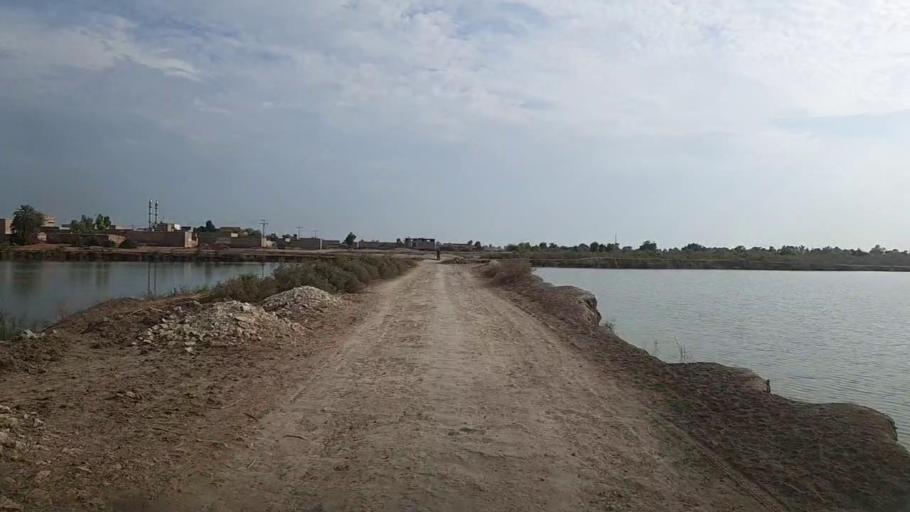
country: PK
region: Sindh
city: Thul
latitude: 28.2706
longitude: 68.8537
